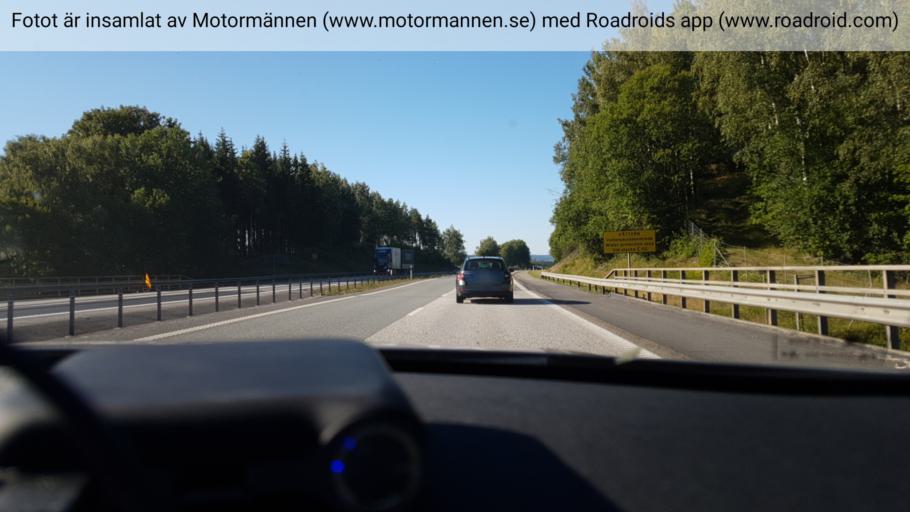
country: SE
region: Joenkoeping
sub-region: Jonkopings Kommun
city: Odensjo
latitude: 57.7270
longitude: 14.1596
